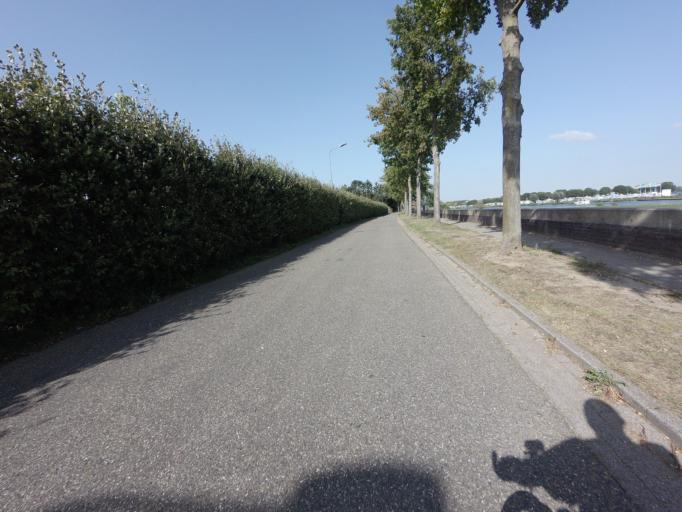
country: NL
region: Limburg
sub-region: Gemeente Roermond
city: Roermond
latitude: 51.1860
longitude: 5.9579
